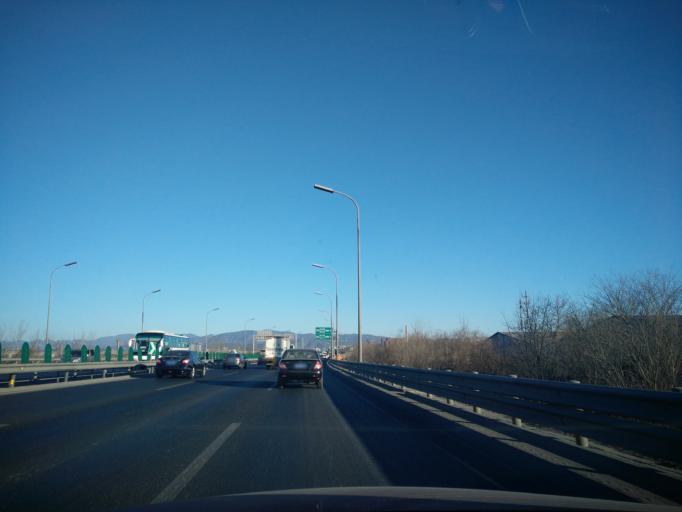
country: CN
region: Beijing
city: Lugu
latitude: 39.8718
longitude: 116.2031
